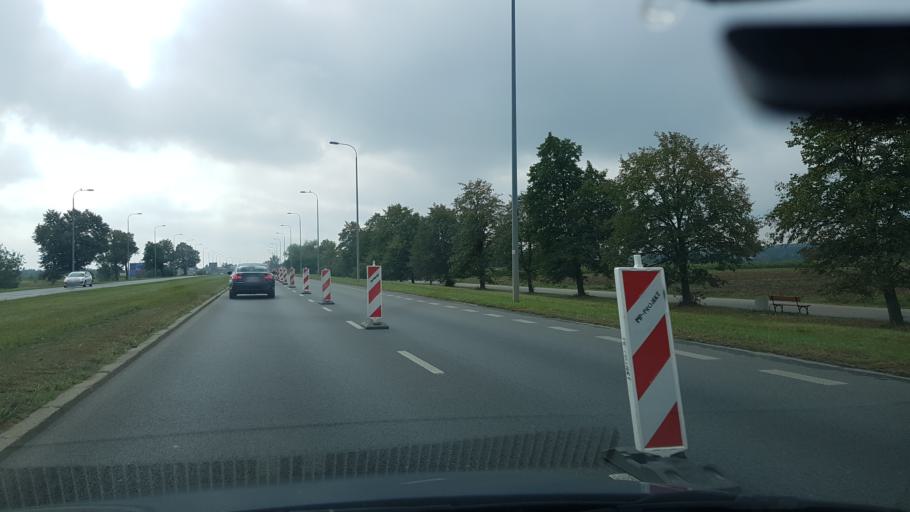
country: PL
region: Masovian Voivodeship
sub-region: Warszawa
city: Kabaty
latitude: 52.1417
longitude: 21.0969
